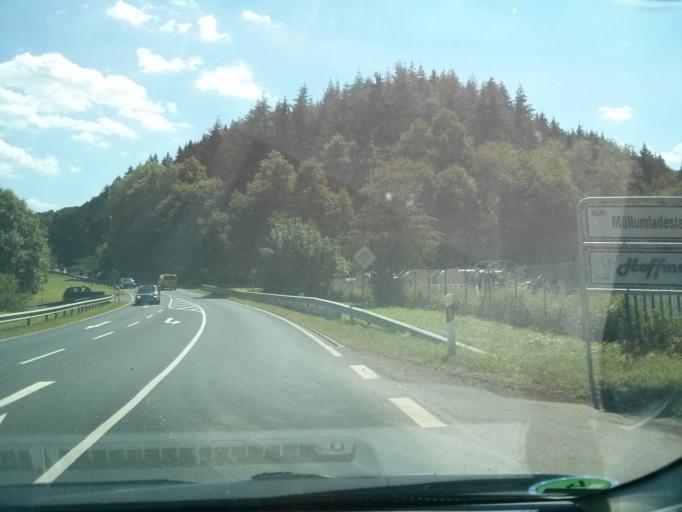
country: DE
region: Rheinland-Pfalz
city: Leimbach
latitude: 50.3936
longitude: 6.9189
